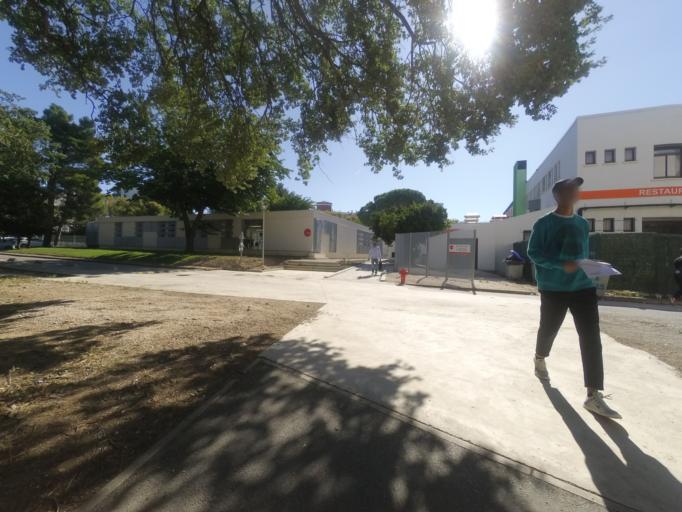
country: FR
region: Languedoc-Roussillon
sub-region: Departement des Pyrenees-Orientales
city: Perpignan
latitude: 42.6819
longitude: 2.9009
